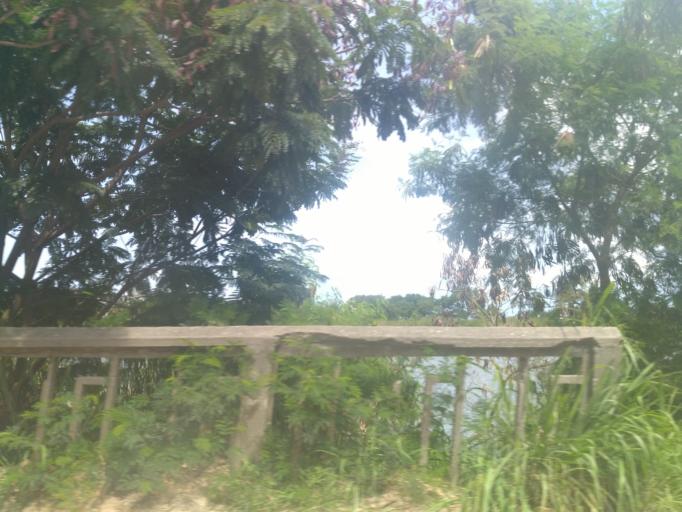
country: TZ
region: Zanzibar Urban/West
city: Zanzibar
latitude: -6.1590
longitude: 39.2010
